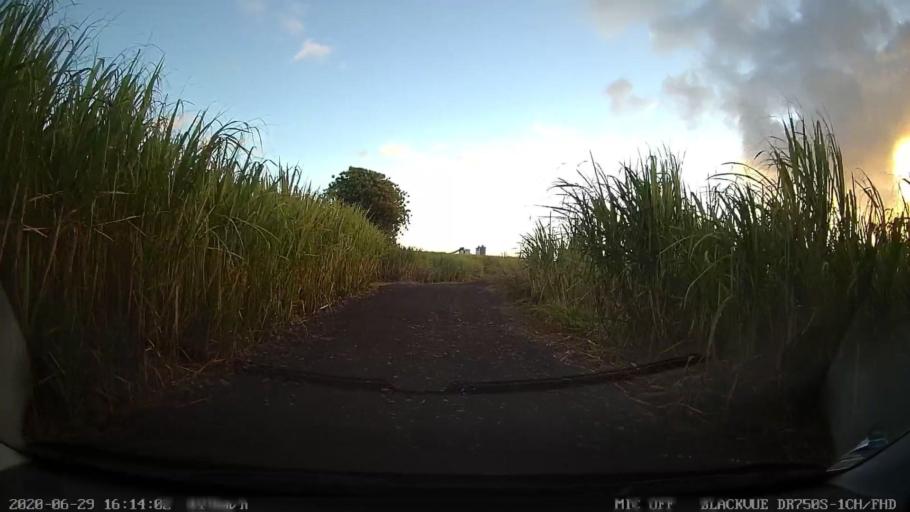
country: RE
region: Reunion
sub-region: Reunion
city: Bras-Panon
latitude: -20.9899
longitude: 55.6965
